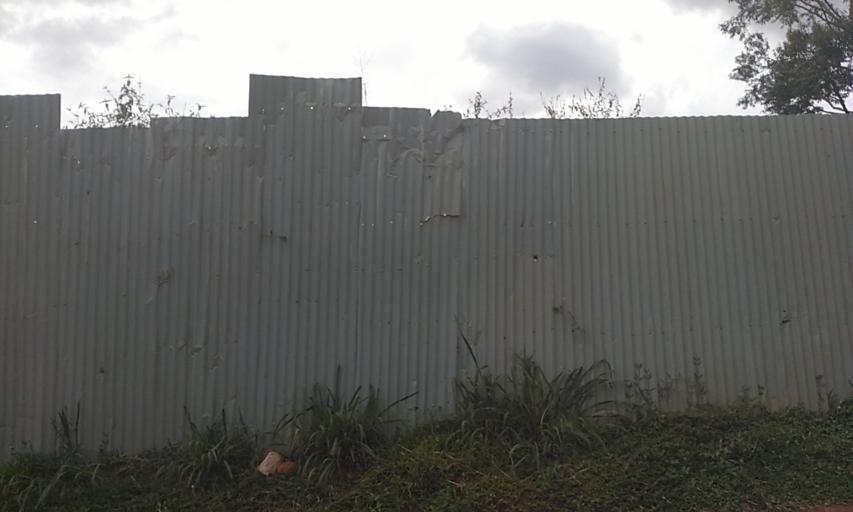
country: UG
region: Central Region
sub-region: Kampala District
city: Kampala
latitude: 0.3346
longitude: 32.6109
